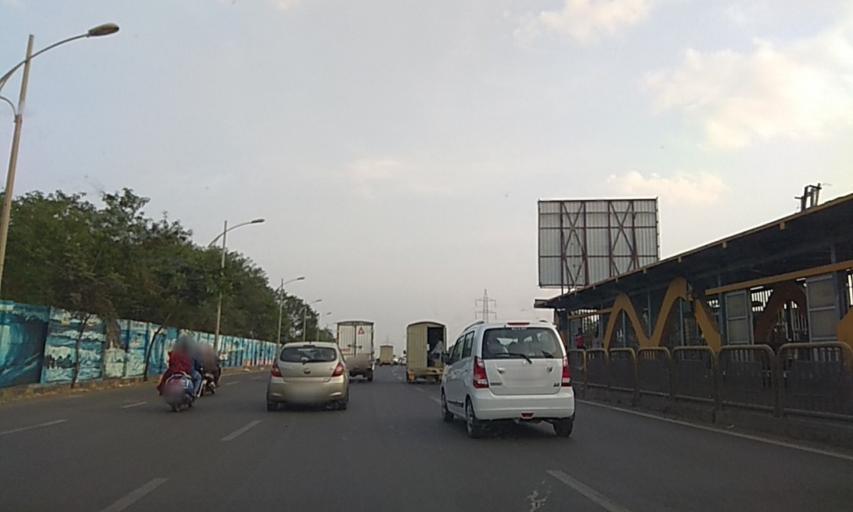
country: IN
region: Maharashtra
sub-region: Pune Division
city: Pimpri
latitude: 18.5813
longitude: 73.7987
